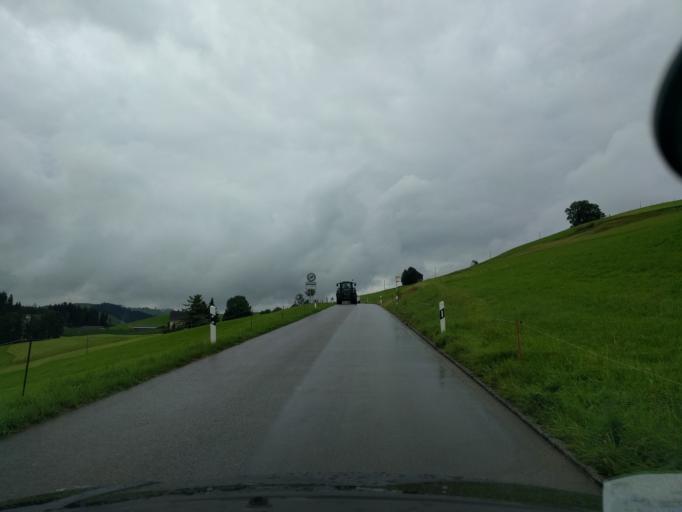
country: CH
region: Saint Gallen
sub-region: Wahlkreis Toggenburg
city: Sankt Peterzell
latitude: 47.3059
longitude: 9.1960
